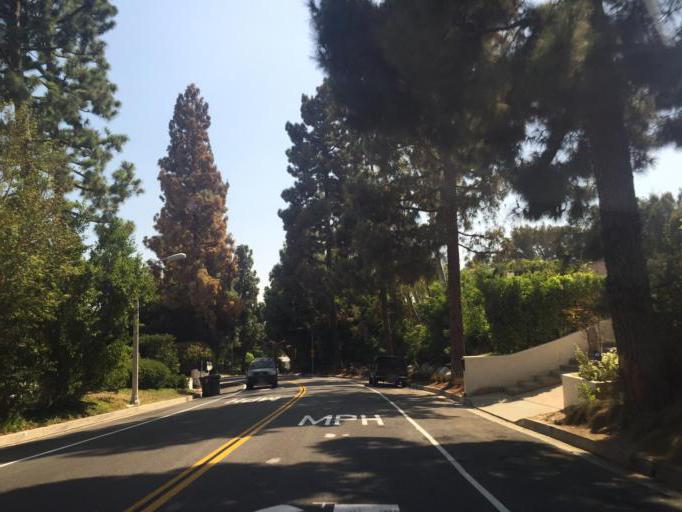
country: US
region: California
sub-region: Los Angeles County
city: Beverly Hills
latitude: 34.0943
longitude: -118.3990
